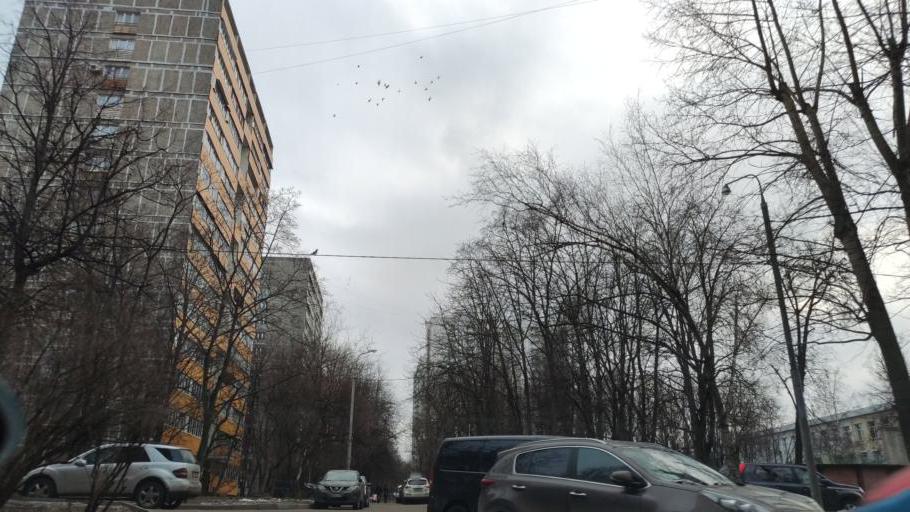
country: RU
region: Moscow
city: Nagornyy
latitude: 55.6309
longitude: 37.6065
